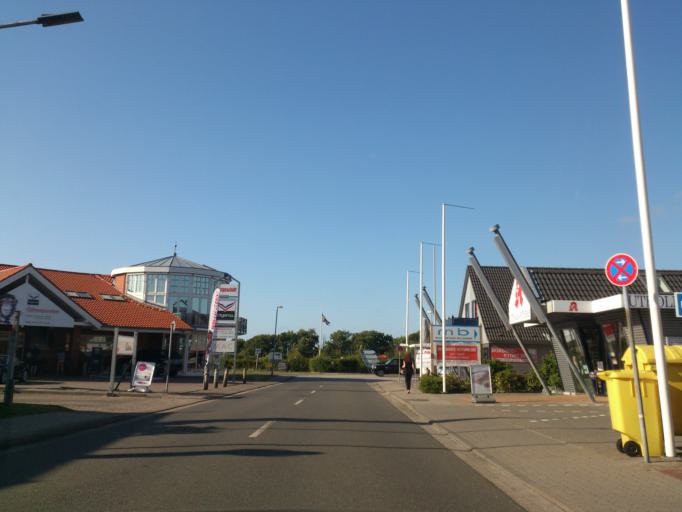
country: DE
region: Schleswig-Holstein
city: Sankt Peter-Ording
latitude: 54.3061
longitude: 8.6475
